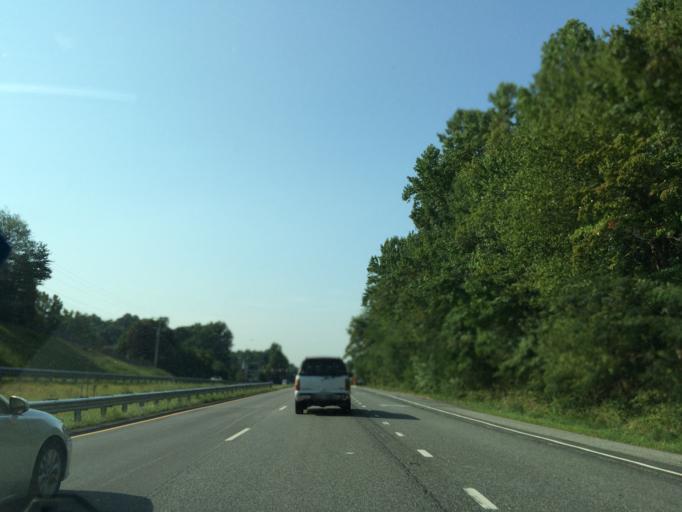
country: US
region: Maryland
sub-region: Prince George's County
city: Marlboro Meadows
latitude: 38.8548
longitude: -76.7260
